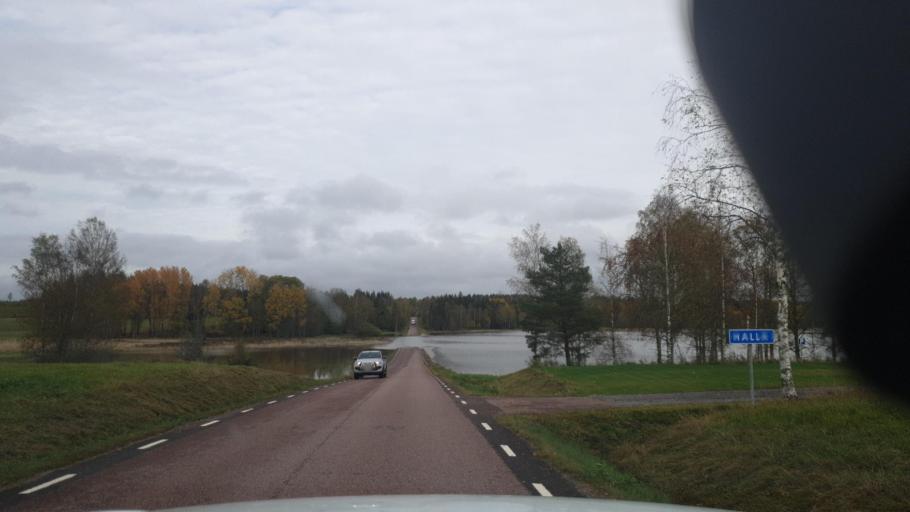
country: SE
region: Vaermland
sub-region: Karlstads Kommun
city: Edsvalla
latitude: 59.4887
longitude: 13.0942
